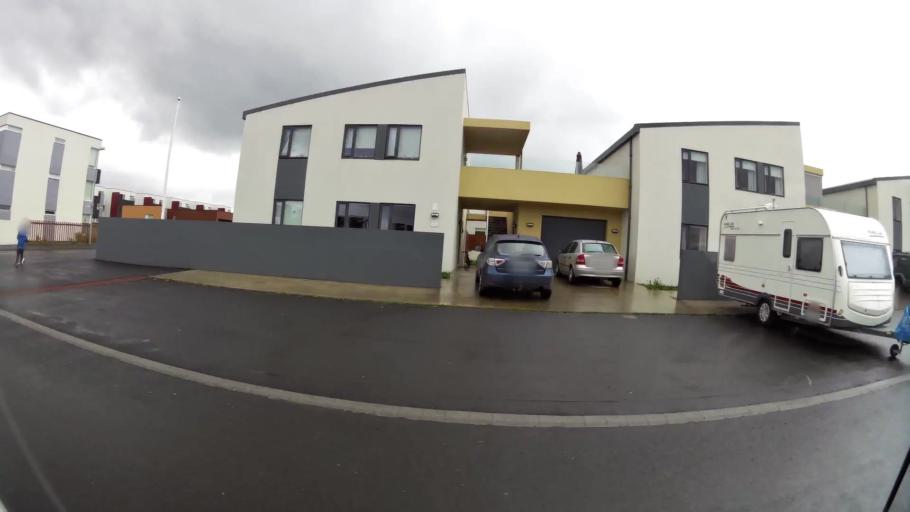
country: IS
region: Northeast
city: Akureyri
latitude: 65.6638
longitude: -18.1026
